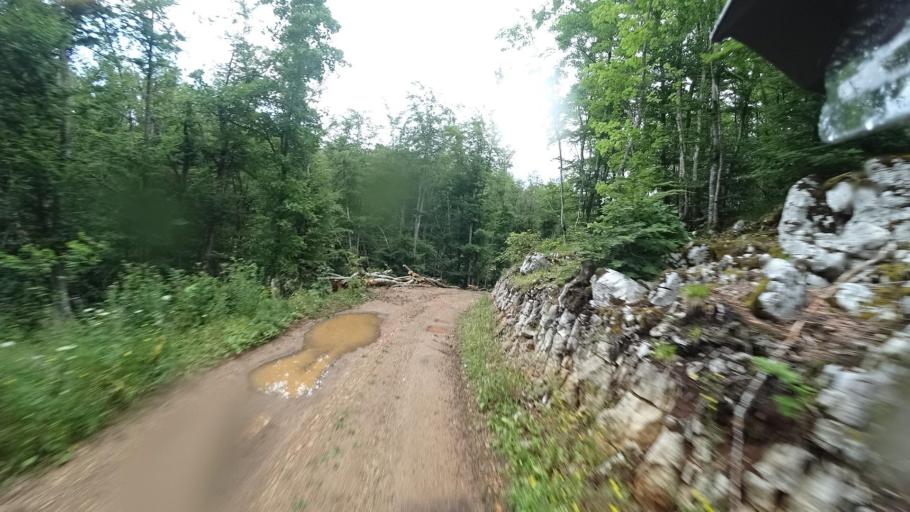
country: HR
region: Licko-Senjska
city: Jezerce
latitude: 44.7319
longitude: 15.6431
